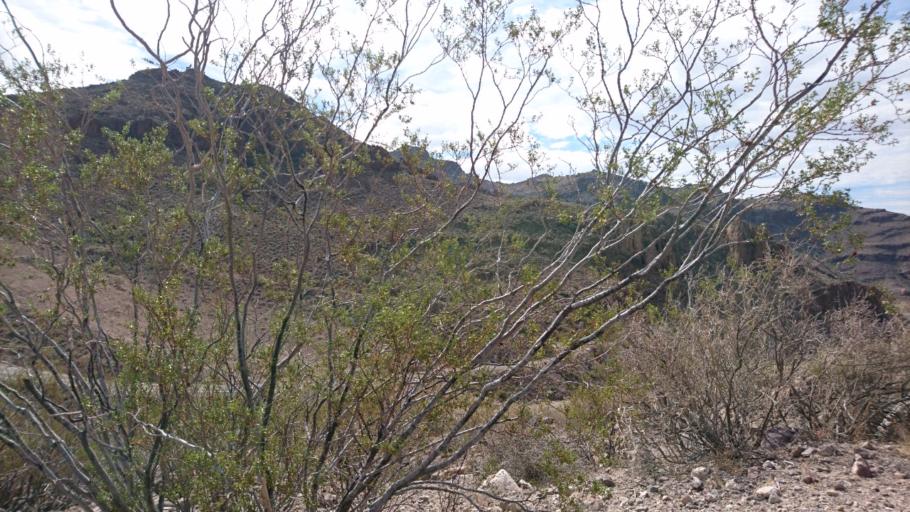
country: US
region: Arizona
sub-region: Mohave County
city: Golden Valley
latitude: 35.0469
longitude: -114.3637
